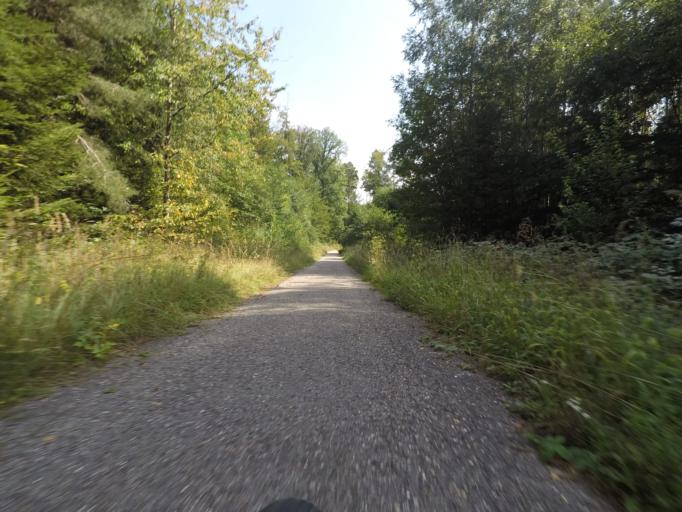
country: DE
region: Baden-Wuerttemberg
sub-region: Regierungsbezirk Stuttgart
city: Steinenbronn
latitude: 48.7067
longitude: 9.0882
